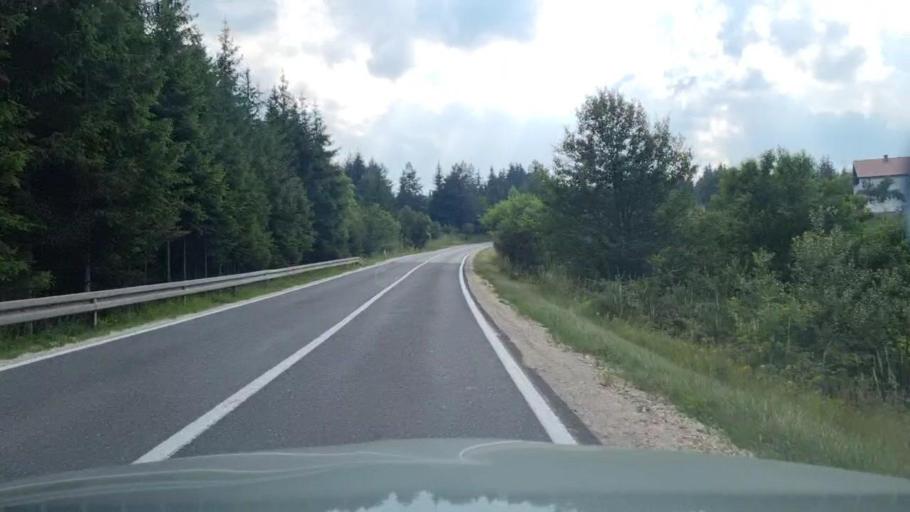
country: BA
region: Federation of Bosnia and Herzegovina
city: Olovo
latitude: 44.0681
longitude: 18.4953
